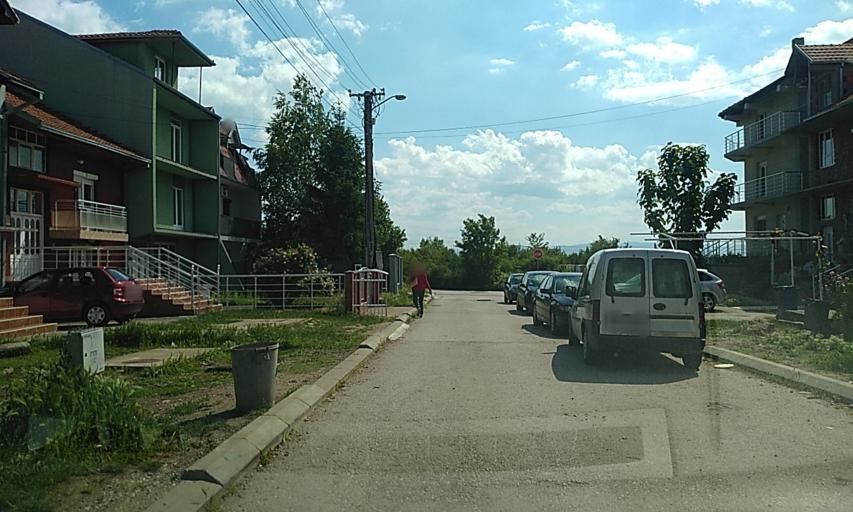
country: RS
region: Central Serbia
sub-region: Nisavski Okrug
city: Nis
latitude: 43.3071
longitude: 21.8657
